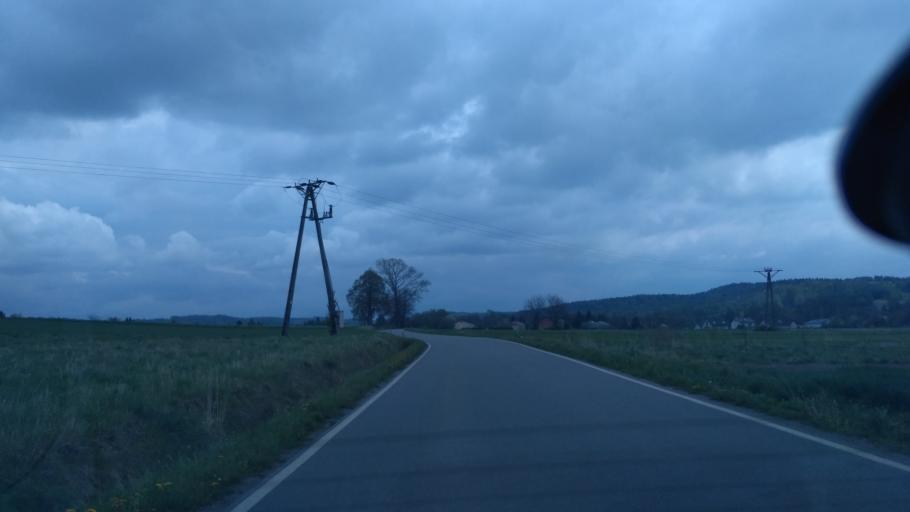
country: PL
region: Subcarpathian Voivodeship
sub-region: Powiat brzozowski
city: Jablonica Polska
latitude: 49.6997
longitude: 21.8868
